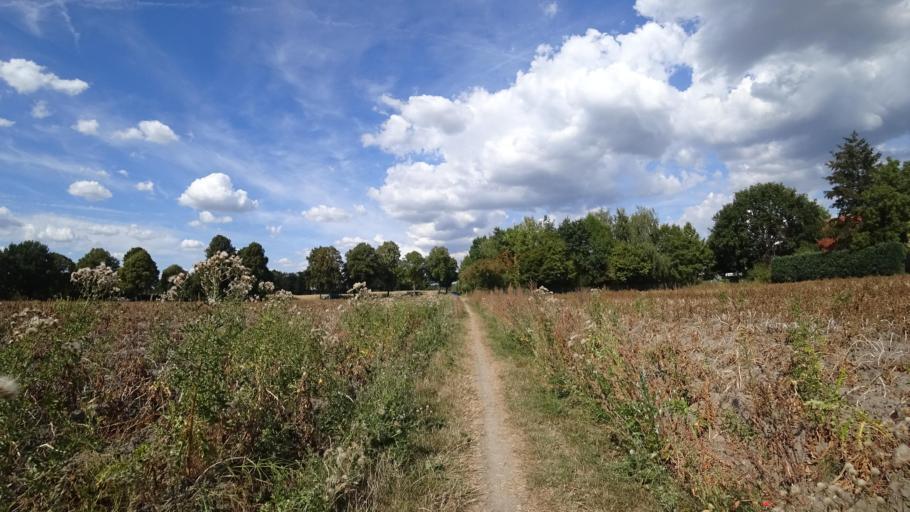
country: DE
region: North Rhine-Westphalia
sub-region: Regierungsbezirk Detmold
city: Verl
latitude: 51.9421
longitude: 8.4910
